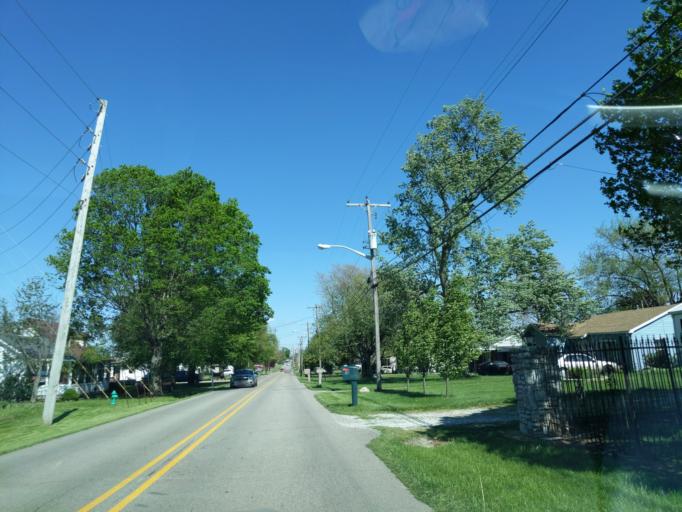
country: US
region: Indiana
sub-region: Decatur County
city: Greensburg
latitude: 39.3292
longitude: -85.4953
